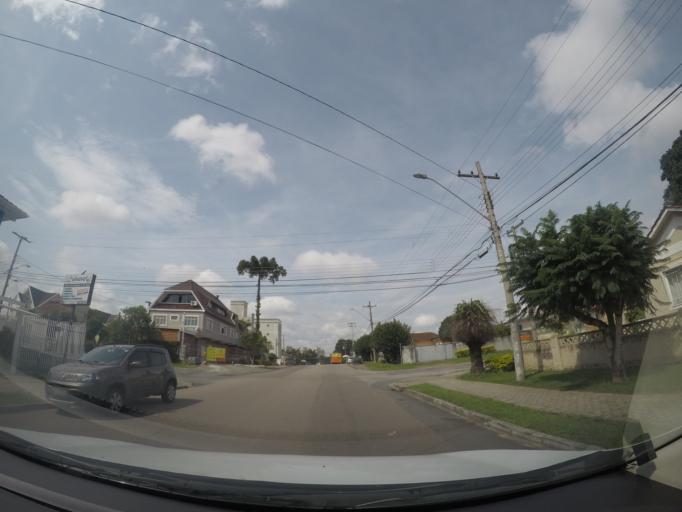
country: BR
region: Parana
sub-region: Curitiba
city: Curitiba
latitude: -25.4908
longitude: -49.2786
